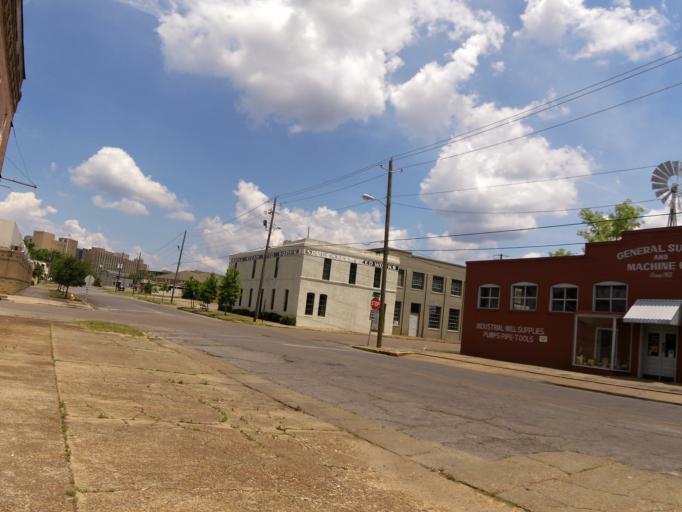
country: US
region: Mississippi
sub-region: Lauderdale County
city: Meridian
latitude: 32.3648
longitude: -88.6967
